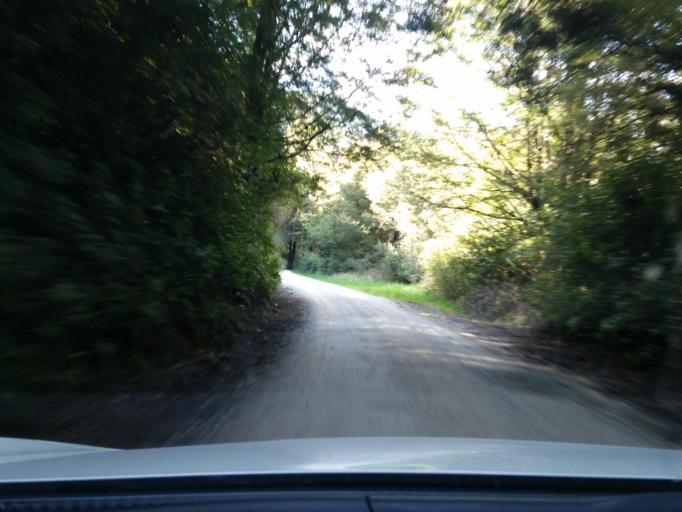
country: NZ
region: West Coast
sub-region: Buller District
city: Westport
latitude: -41.7721
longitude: 172.2271
